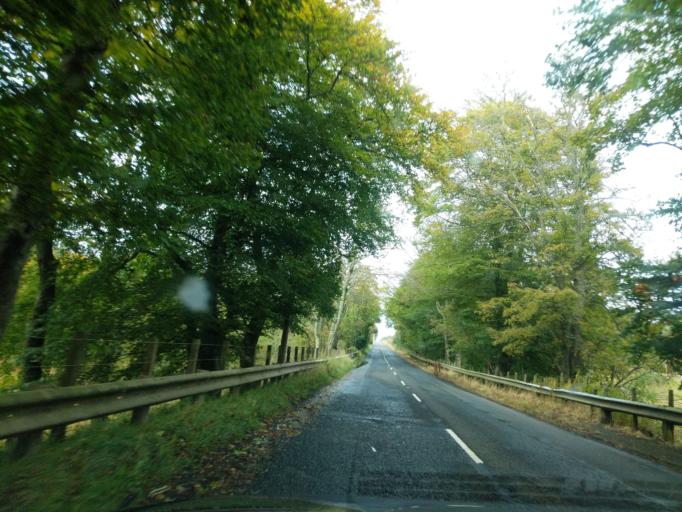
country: GB
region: Scotland
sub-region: Midlothian
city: Penicuik
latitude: 55.8183
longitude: -3.2754
